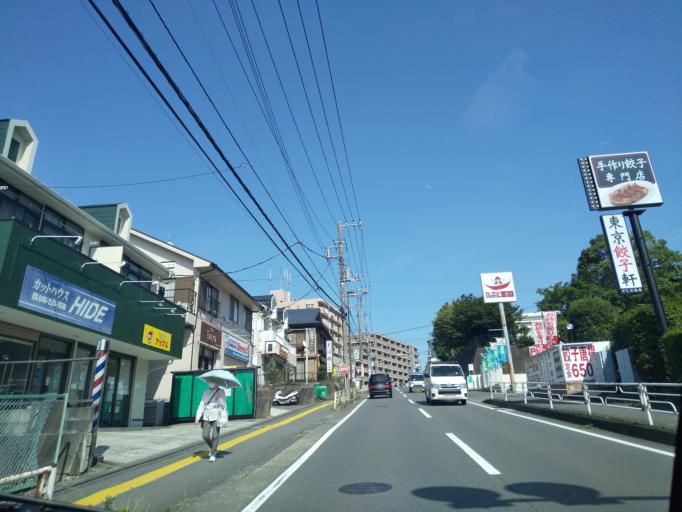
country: JP
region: Kanagawa
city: Zama
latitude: 35.4686
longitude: 139.4119
